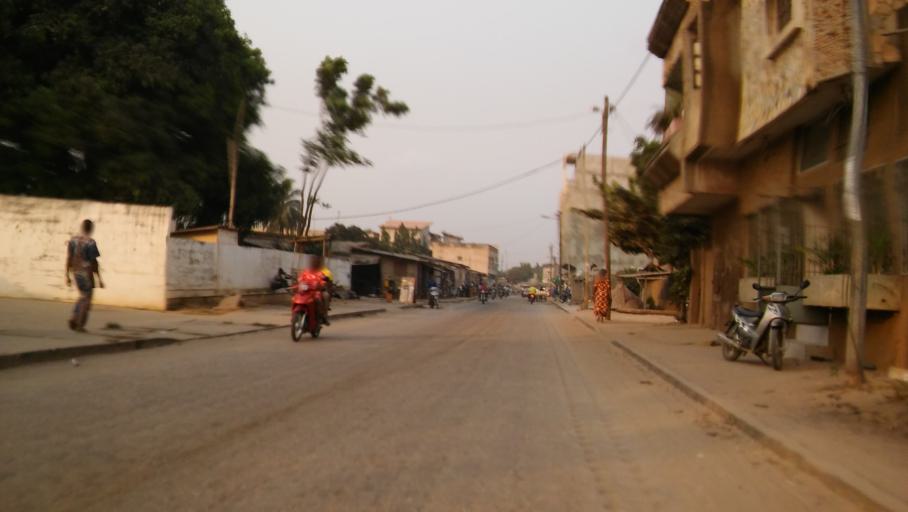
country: BJ
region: Atlantique
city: Abomey-Calavi
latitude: 6.3850
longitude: 2.3427
